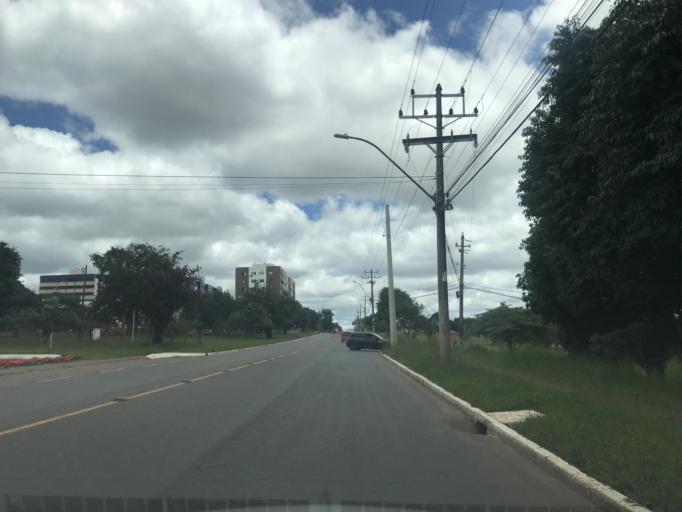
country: BR
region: Federal District
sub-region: Brasilia
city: Brasilia
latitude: -15.6537
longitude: -47.7926
